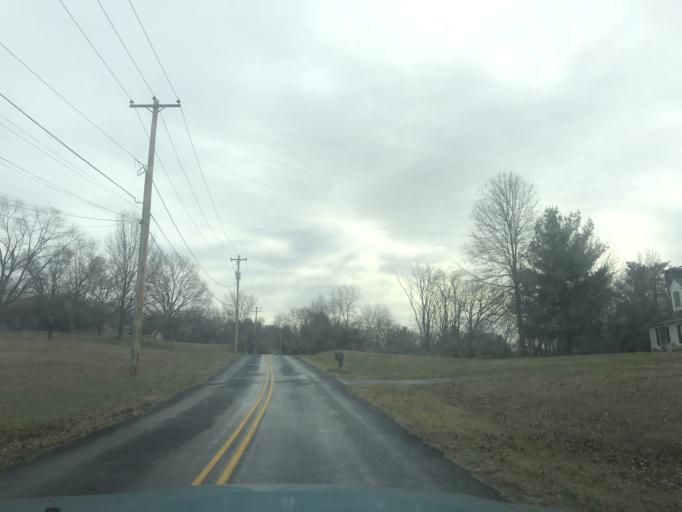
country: US
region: Pennsylvania
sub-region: Montgomery County
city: Harleysville
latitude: 40.2678
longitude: -75.4087
